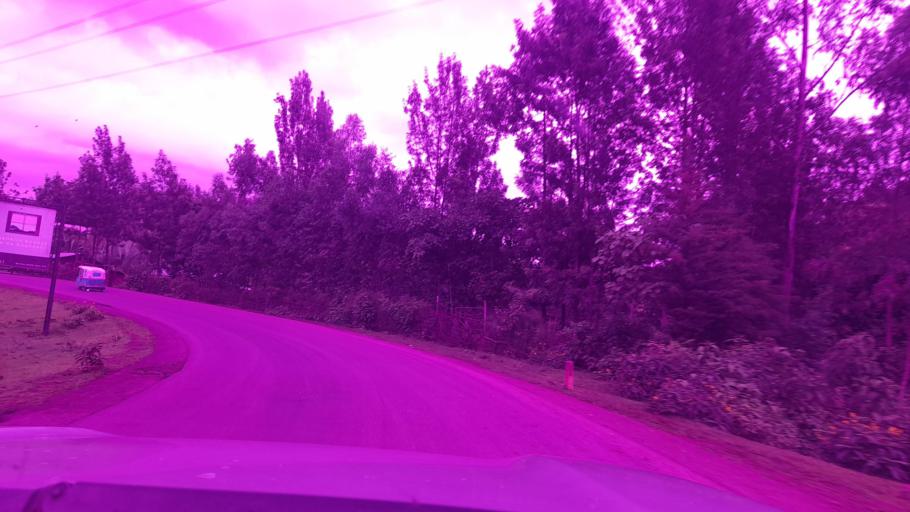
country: ET
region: Oromiya
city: Jima
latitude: 7.9183
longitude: 37.4077
